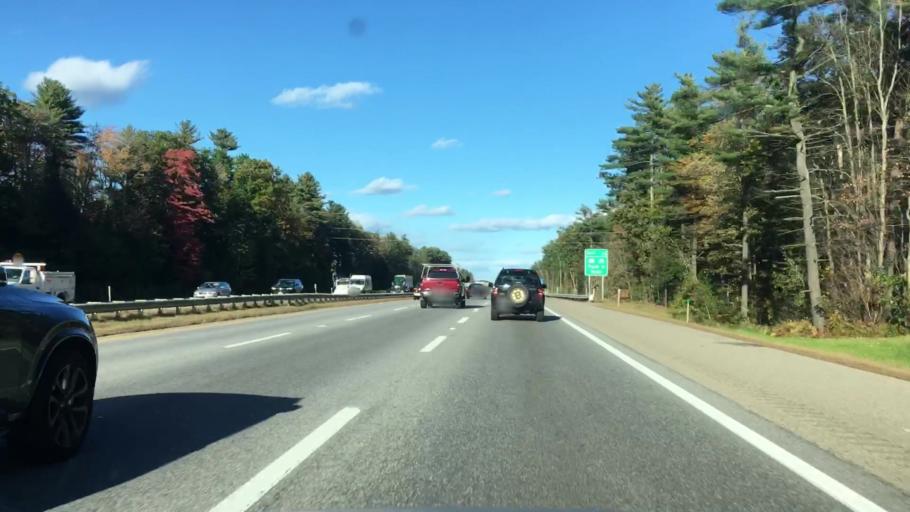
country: US
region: Maine
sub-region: York County
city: Biddeford
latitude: 43.5088
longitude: -70.4773
